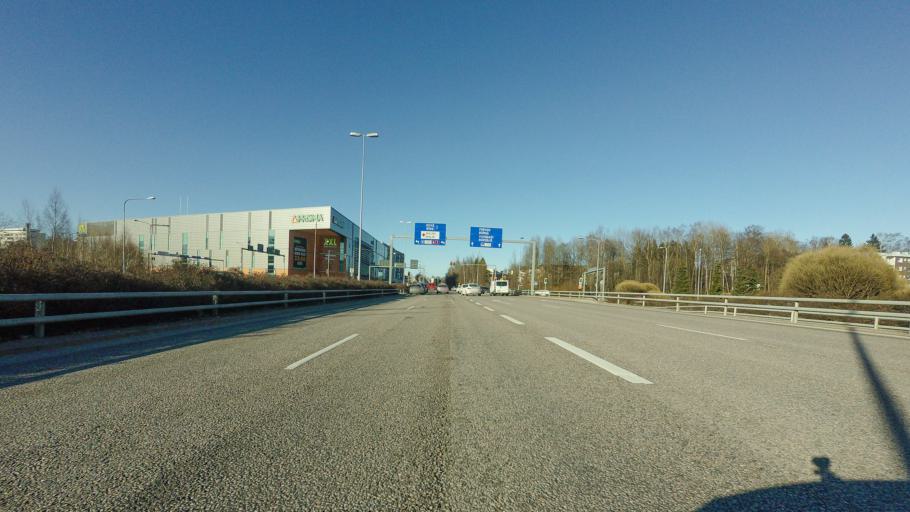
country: FI
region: Uusimaa
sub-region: Helsinki
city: Vantaa
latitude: 60.2117
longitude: 25.0864
